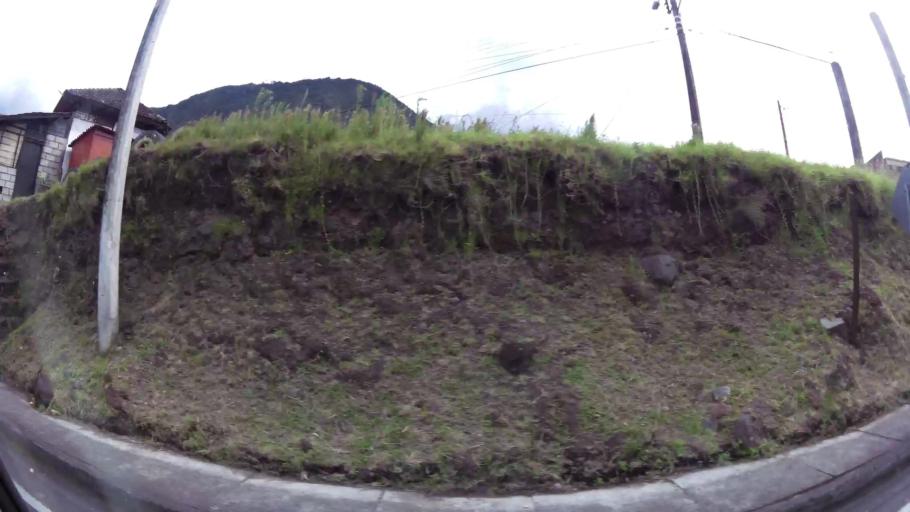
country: EC
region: Tungurahua
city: Banos
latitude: -1.3966
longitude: -78.4290
